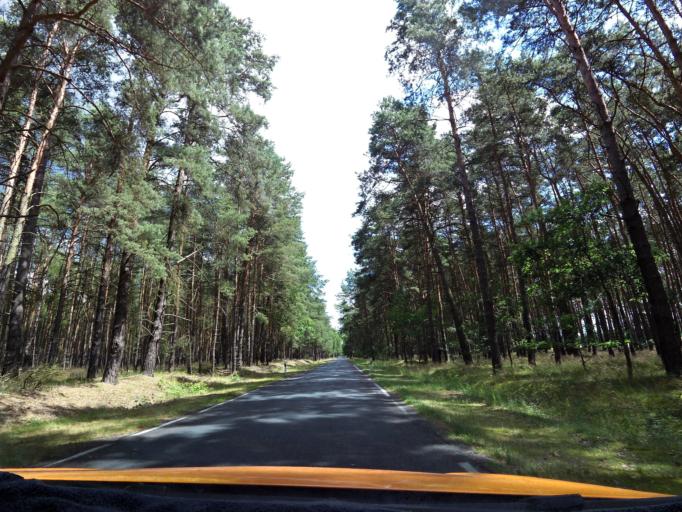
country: DE
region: Brandenburg
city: Storkow
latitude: 52.2457
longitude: 13.8459
